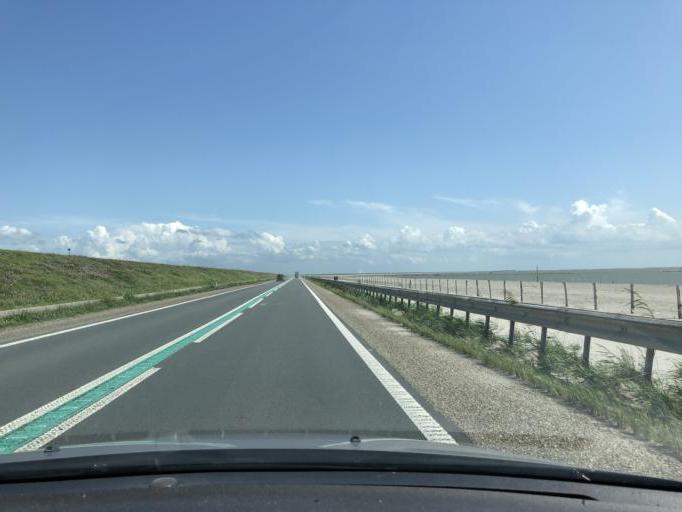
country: NL
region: North Holland
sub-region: Gemeente Enkhuizen
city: Enkhuizen
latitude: 52.6815
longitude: 5.3381
